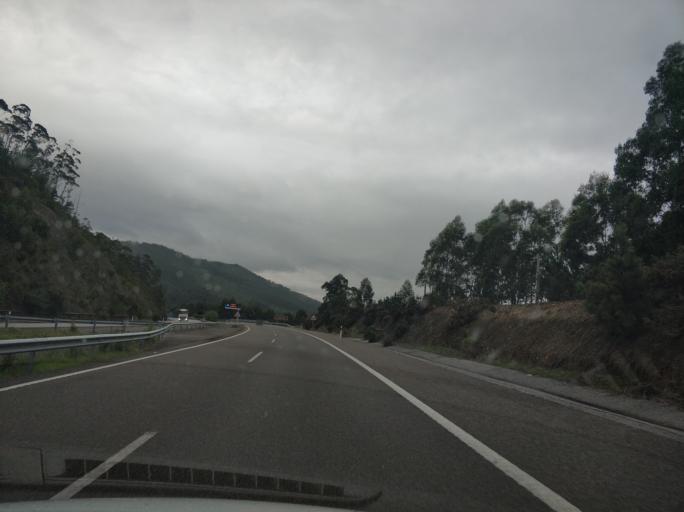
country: ES
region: Galicia
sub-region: Provincia de Lugo
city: Ribadeo
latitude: 43.5358
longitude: -7.1301
